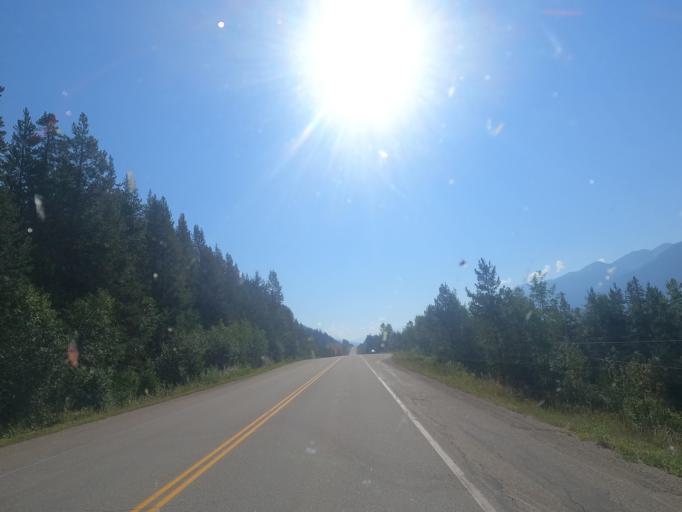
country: CA
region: Alberta
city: Jasper Park Lodge
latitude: 52.9710
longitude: -118.9368
